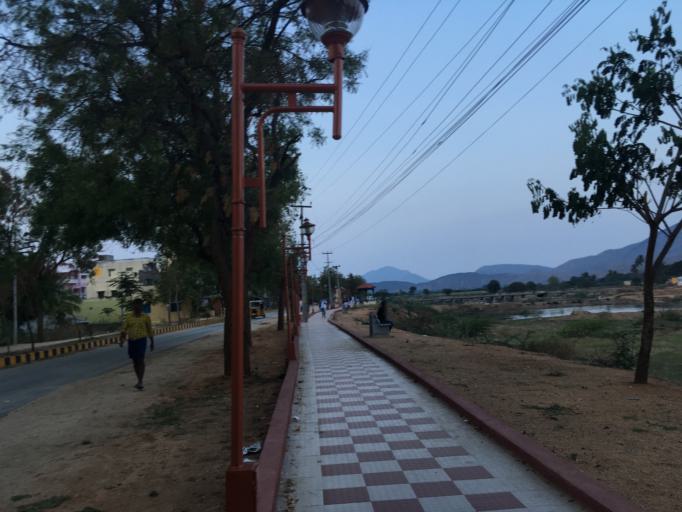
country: IN
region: Andhra Pradesh
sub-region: Anantapur
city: Puttaparthi
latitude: 14.1656
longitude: 77.8150
